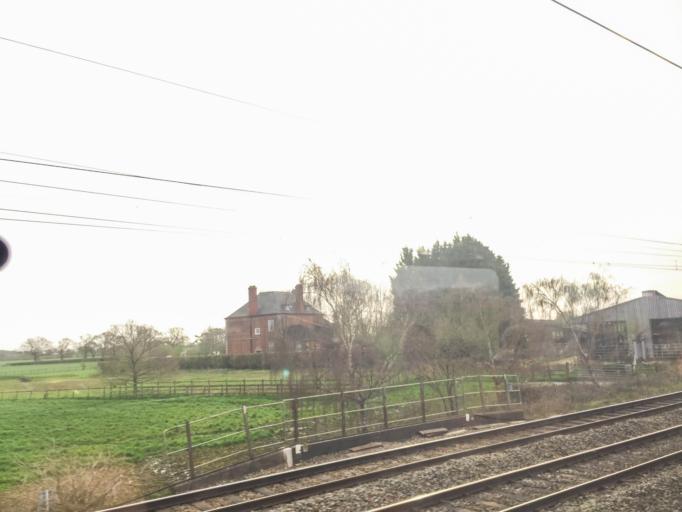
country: GB
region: England
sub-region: Cheshire West and Chester
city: Winsford
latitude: 53.1734
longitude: -2.4811
